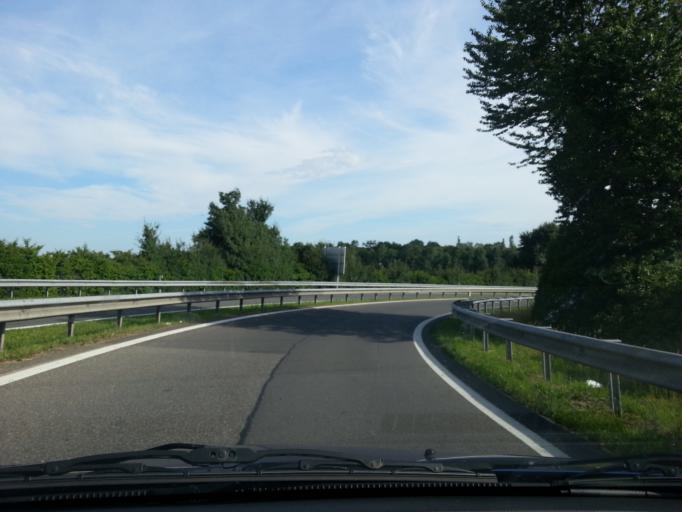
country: AT
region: Styria
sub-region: Politischer Bezirk Leibnitz
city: Gabersdorf
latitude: 46.8085
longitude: 15.5700
